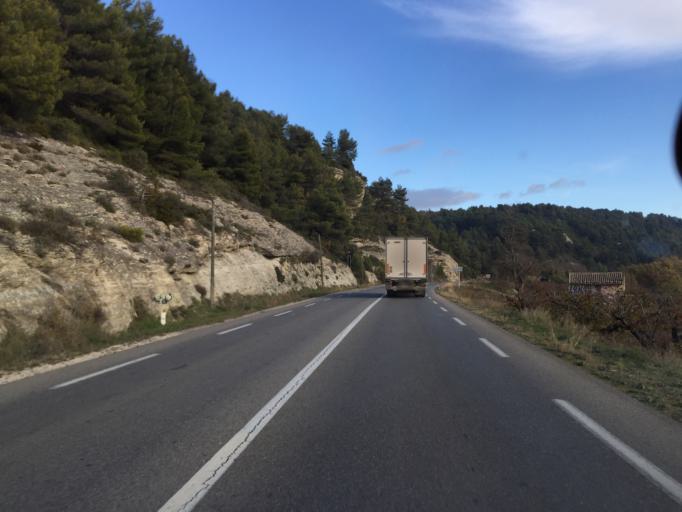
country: FR
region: Provence-Alpes-Cote d'Azur
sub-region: Departement du Vaucluse
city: Goult
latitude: 43.8611
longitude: 5.2170
